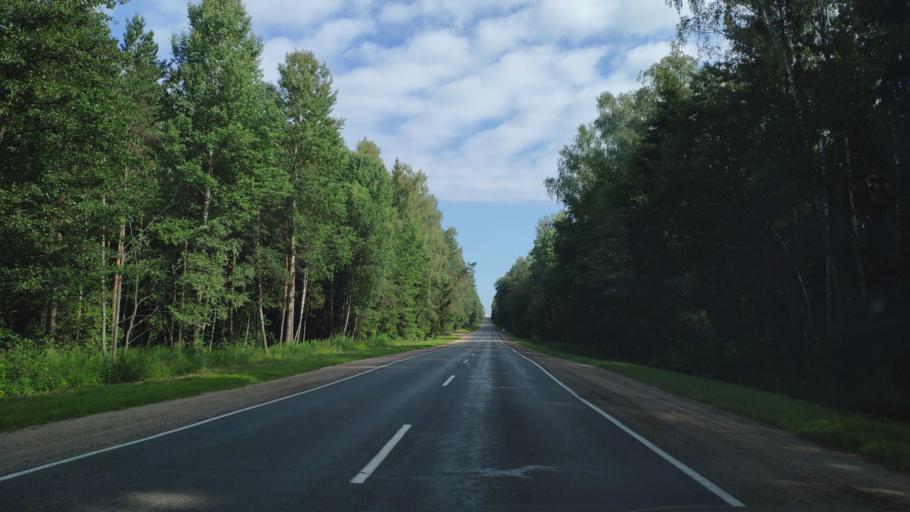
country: BY
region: Minsk
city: Novosel'ye
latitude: 53.9345
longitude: 27.2437
